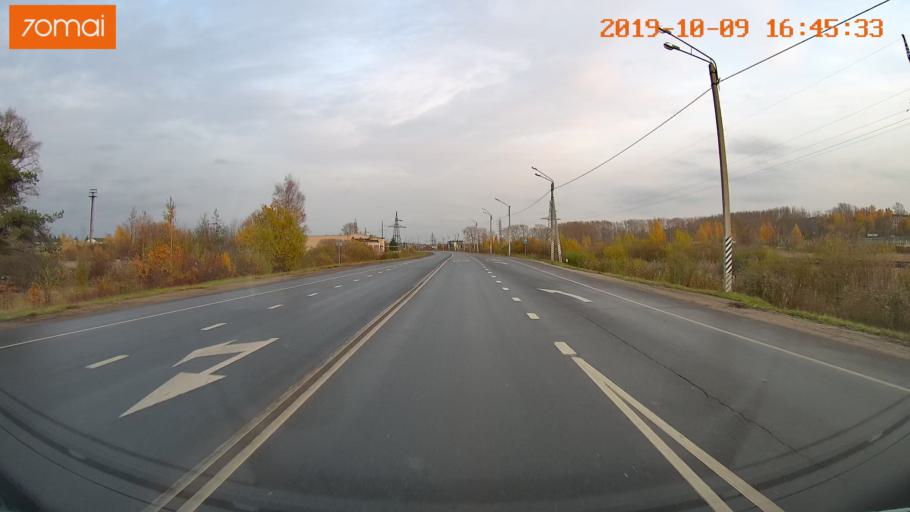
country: RU
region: Kostroma
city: Volgorechensk
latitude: 57.4459
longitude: 41.1567
